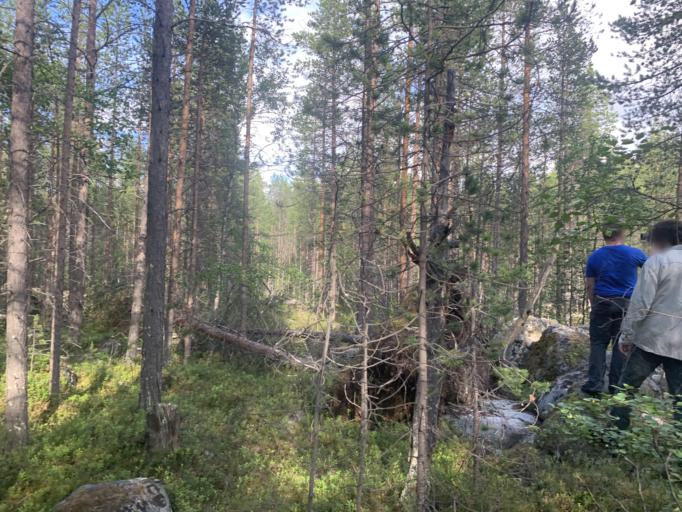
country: RU
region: Murmansk
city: Monchegorsk
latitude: 67.8794
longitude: 33.1050
